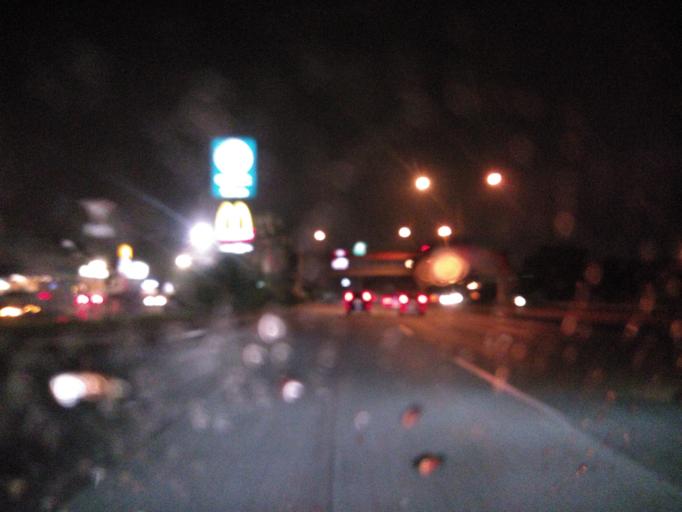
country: MY
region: Penang
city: Perai
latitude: 5.4001
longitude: 100.4009
